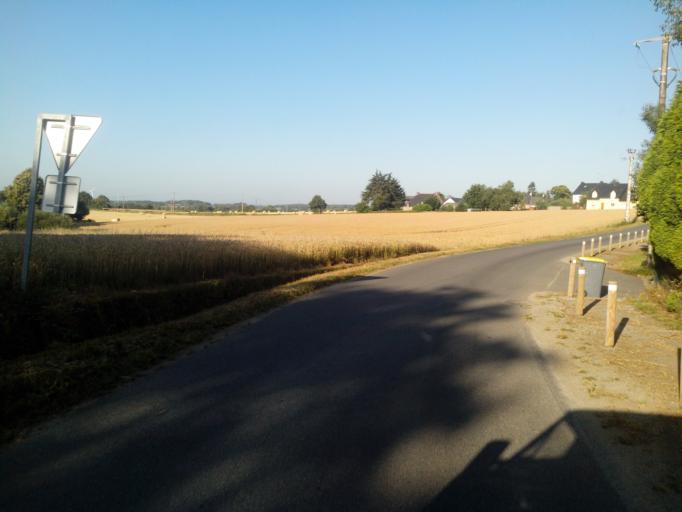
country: FR
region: Brittany
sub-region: Departement du Morbihan
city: Meneac
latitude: 48.1364
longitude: -2.4573
